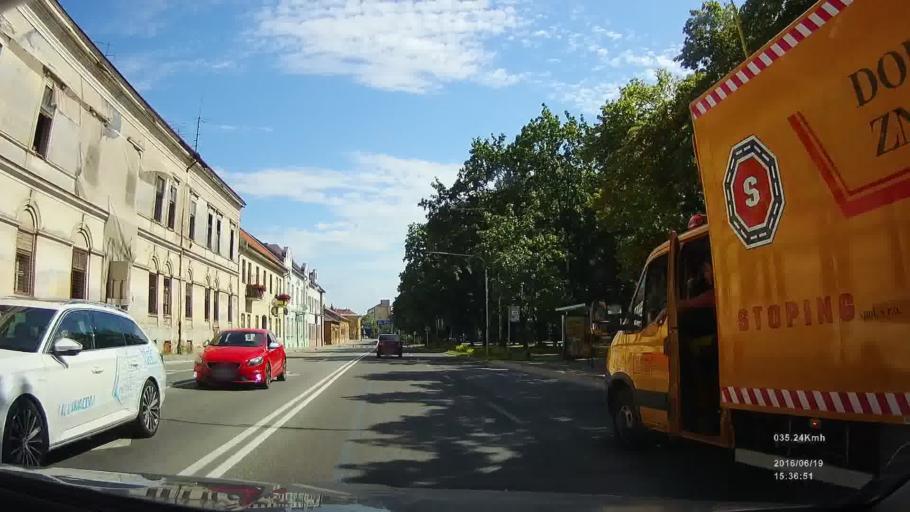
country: SK
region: Kosicky
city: Kosice
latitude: 48.7190
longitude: 21.2527
